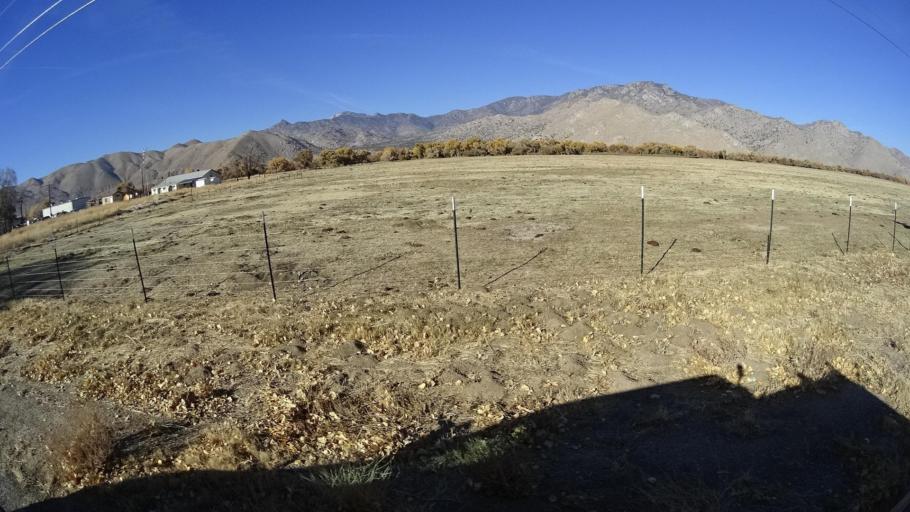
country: US
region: California
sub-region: Kern County
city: Weldon
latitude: 35.6660
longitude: -118.2884
